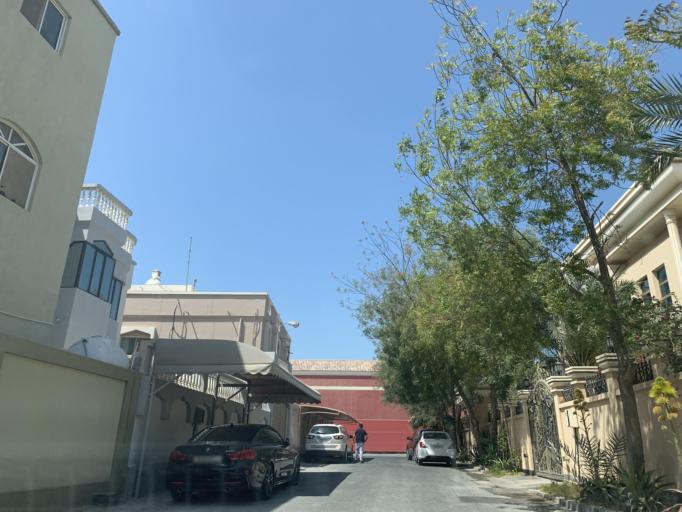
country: BH
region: Manama
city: Manama
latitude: 26.2100
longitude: 50.5728
